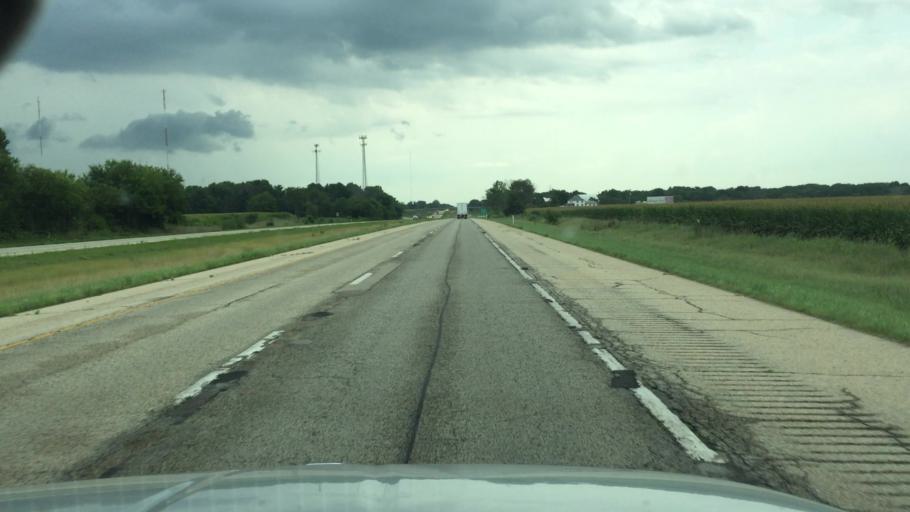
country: US
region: Illinois
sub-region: Peoria County
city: Hanna City
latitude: 40.7787
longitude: -89.7647
